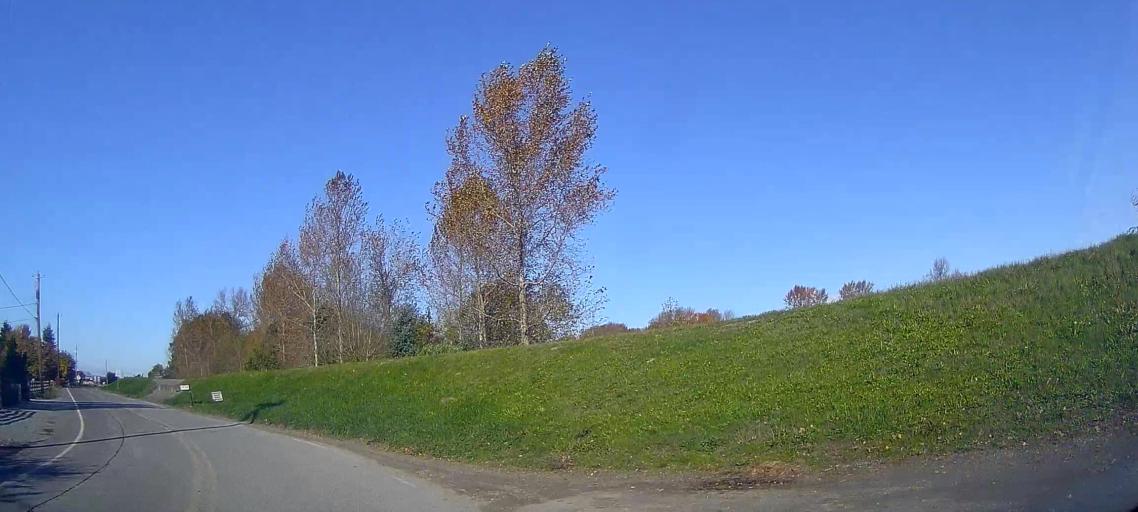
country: US
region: Washington
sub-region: Skagit County
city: Mount Vernon
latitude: 48.3994
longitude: -122.3669
